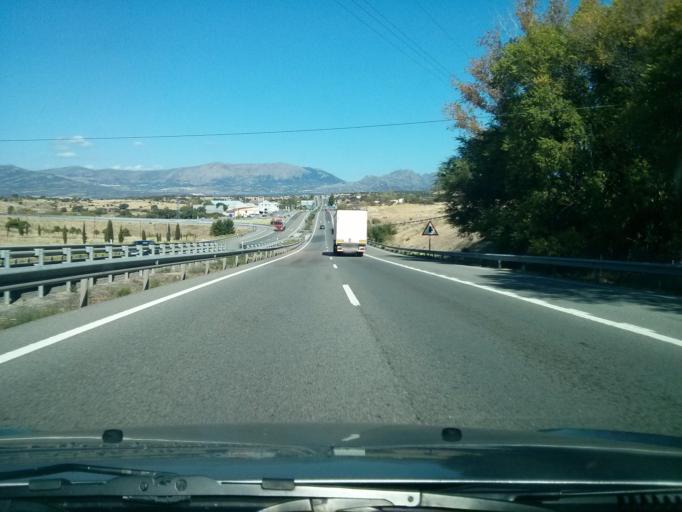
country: ES
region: Madrid
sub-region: Provincia de Madrid
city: Pedrezuela
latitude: 40.7643
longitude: -3.6037
